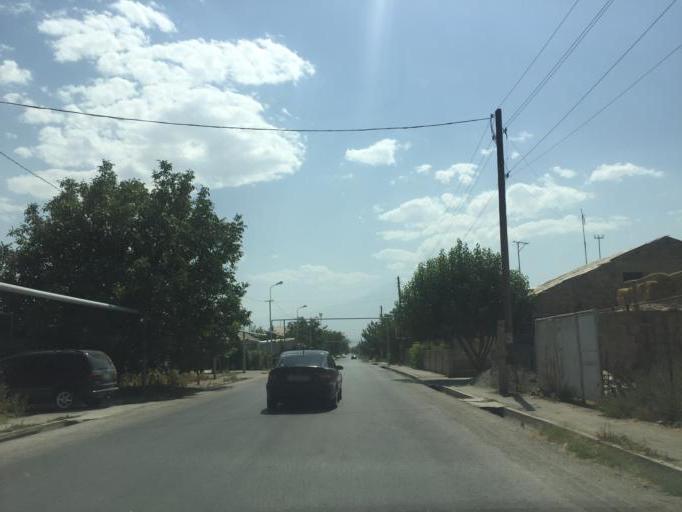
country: AM
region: Ararat
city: Aralez
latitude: 39.9061
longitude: 44.6065
